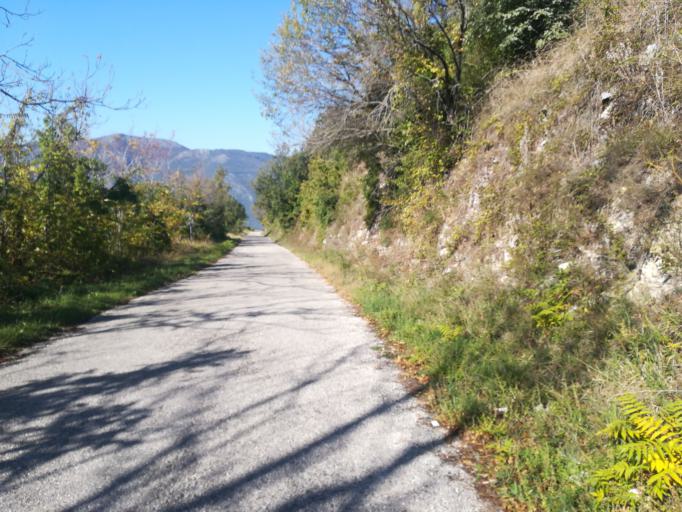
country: IT
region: Umbria
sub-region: Provincia di Perugia
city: Scheggino
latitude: 42.6770
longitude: 12.8479
